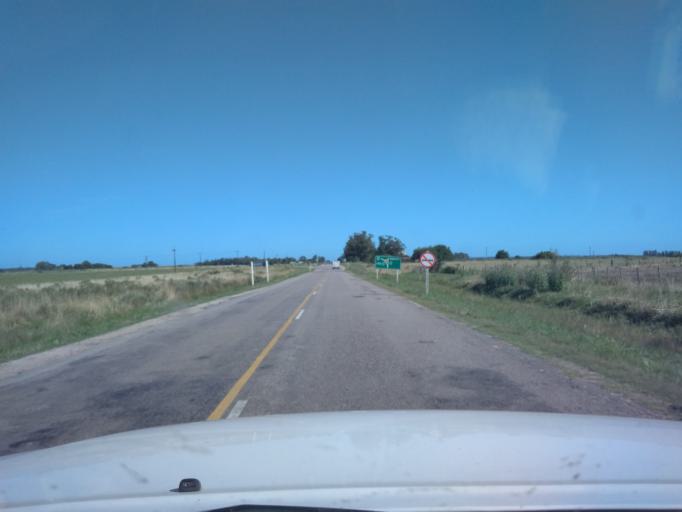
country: UY
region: Canelones
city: San Ramon
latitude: -34.2061
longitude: -55.9317
